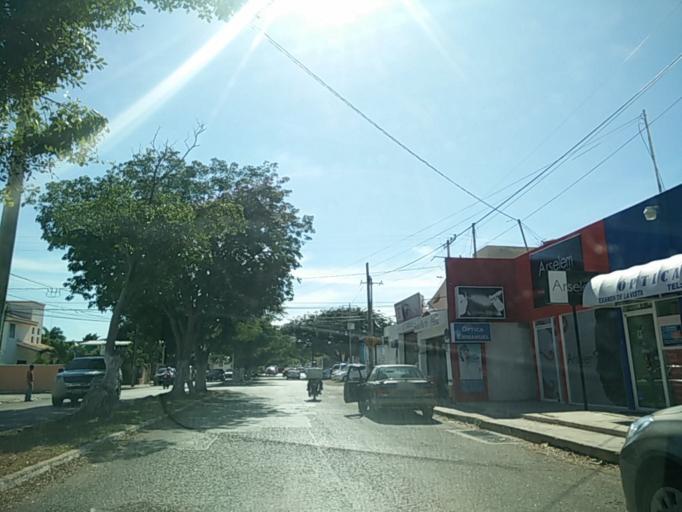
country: MX
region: Yucatan
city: Merida
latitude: 20.9984
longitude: -89.6059
